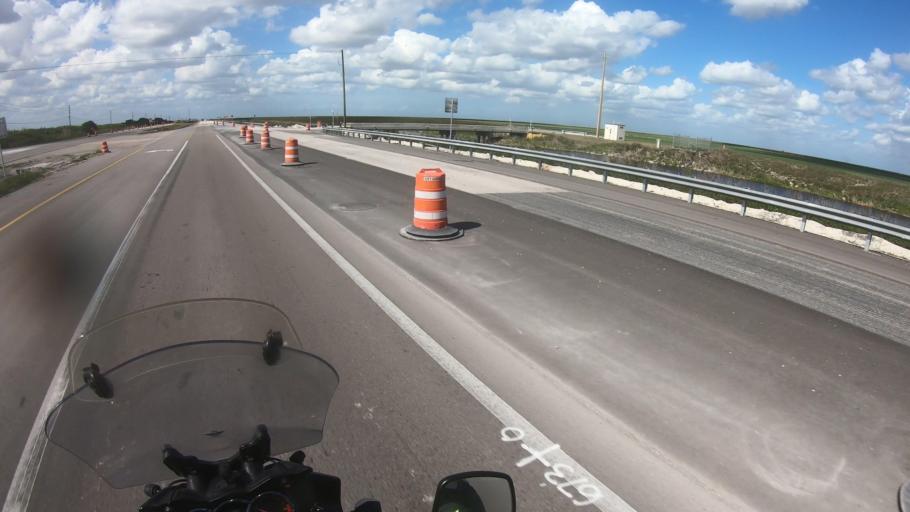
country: US
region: Florida
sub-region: Palm Beach County
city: Belle Glade Camp
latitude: 26.4835
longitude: -80.6515
